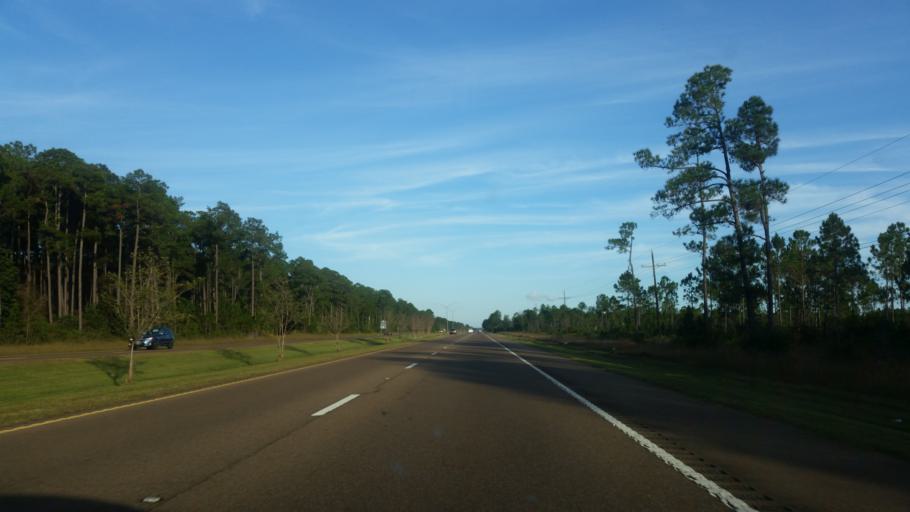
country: US
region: Mississippi
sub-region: Jackson County
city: Gulf Park Estates
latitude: 30.3988
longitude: -88.6971
